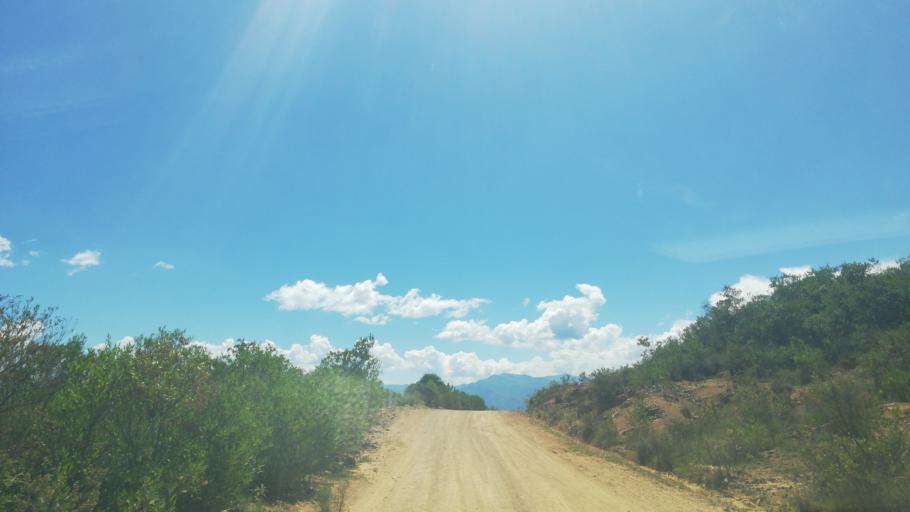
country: BO
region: Cochabamba
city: Totora
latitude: -17.7355
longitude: -65.2250
